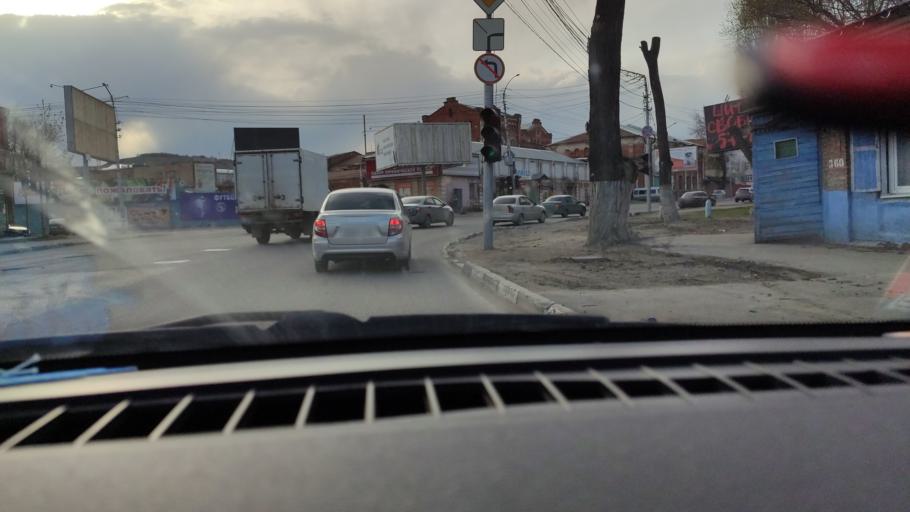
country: RU
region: Saratov
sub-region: Saratovskiy Rayon
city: Saratov
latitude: 51.5508
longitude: 46.0107
